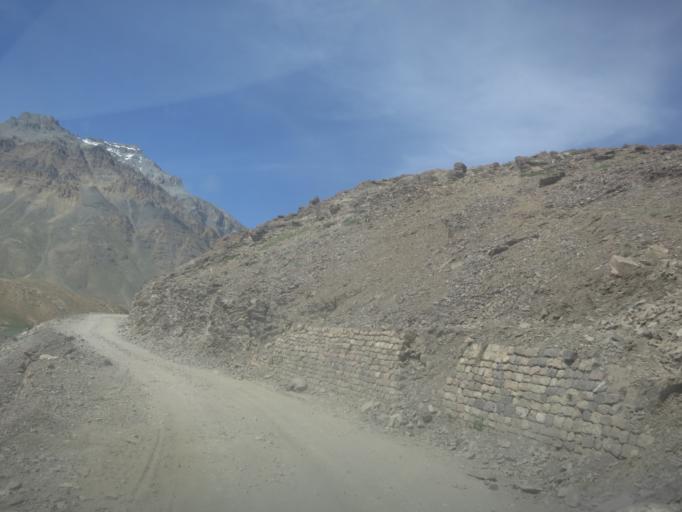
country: IN
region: Himachal Pradesh
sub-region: Kulu
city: Manali
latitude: 32.4488
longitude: 77.6947
